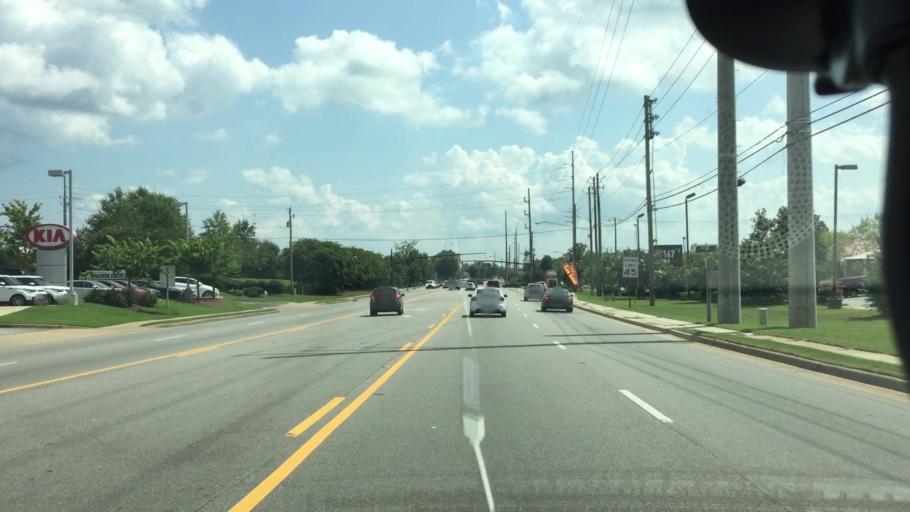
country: US
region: Alabama
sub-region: Lee County
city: Auburn
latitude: 32.5748
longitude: -85.4989
